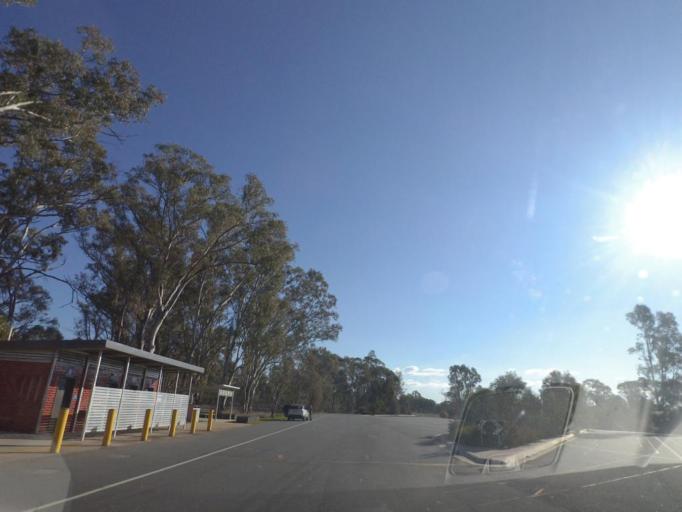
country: AU
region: Victoria
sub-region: Benalla
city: Benalla
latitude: -36.5774
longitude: 145.9212
